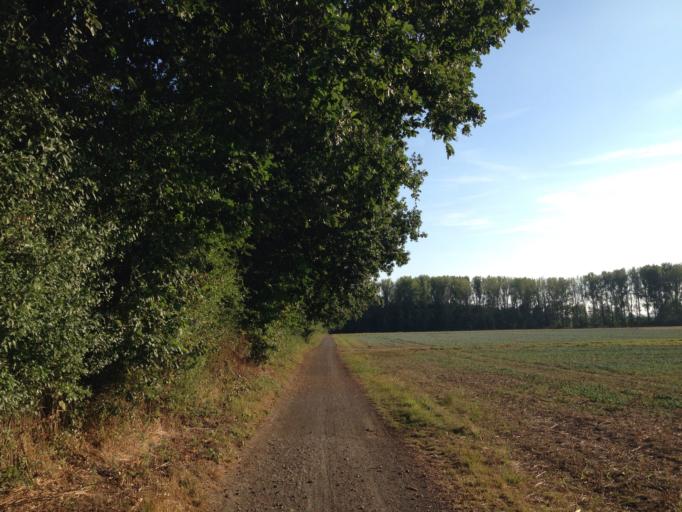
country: DE
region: Hesse
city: Lollar
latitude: 50.6367
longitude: 8.6950
